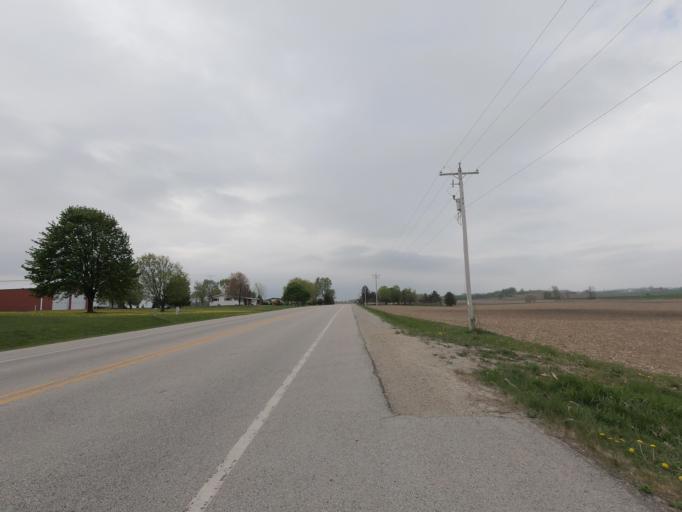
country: US
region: Wisconsin
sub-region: Jefferson County
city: Johnson Creek
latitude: 43.0351
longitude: -88.7735
